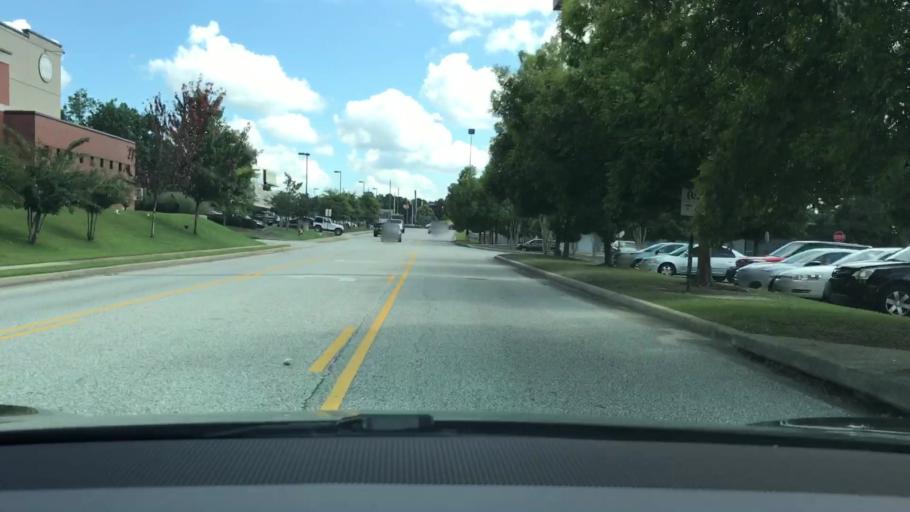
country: US
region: Alabama
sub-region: Lee County
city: Auburn
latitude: 32.6278
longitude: -85.4449
